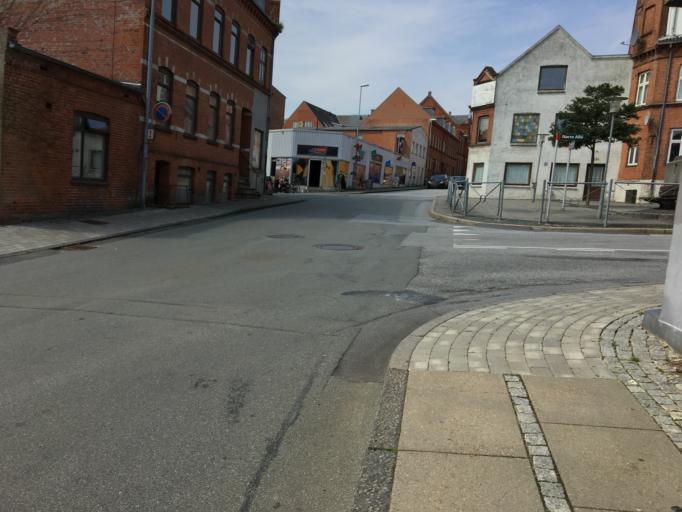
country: DK
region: Central Jutland
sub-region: Skive Kommune
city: Skive
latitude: 56.5685
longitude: 9.0303
